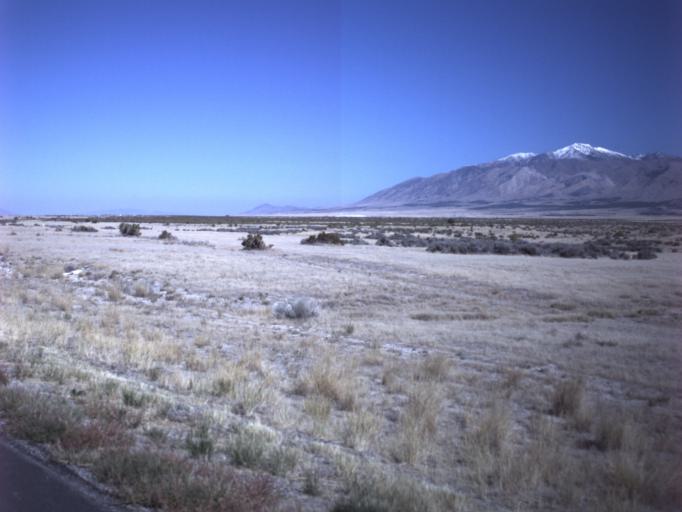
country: US
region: Utah
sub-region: Tooele County
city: Grantsville
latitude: 40.2552
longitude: -112.7394
